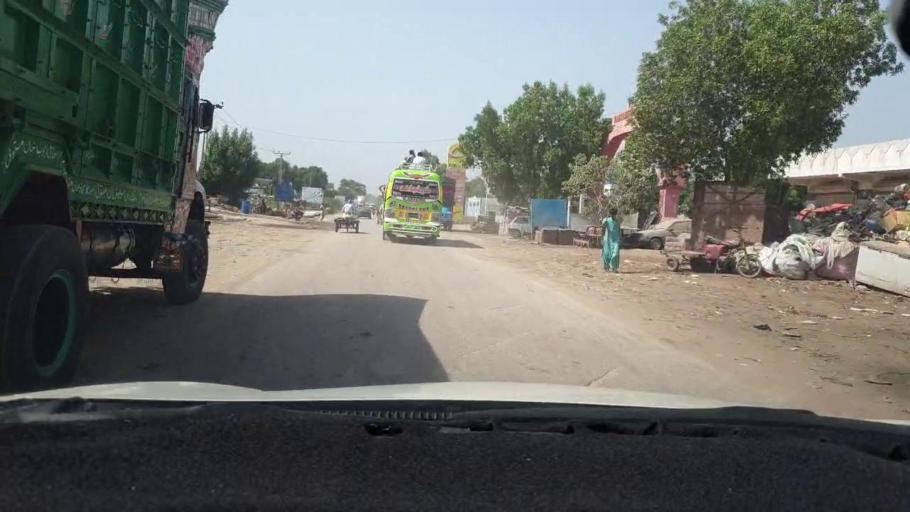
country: PK
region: Sindh
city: Mirpur Khas
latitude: 25.5413
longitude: 69.0350
